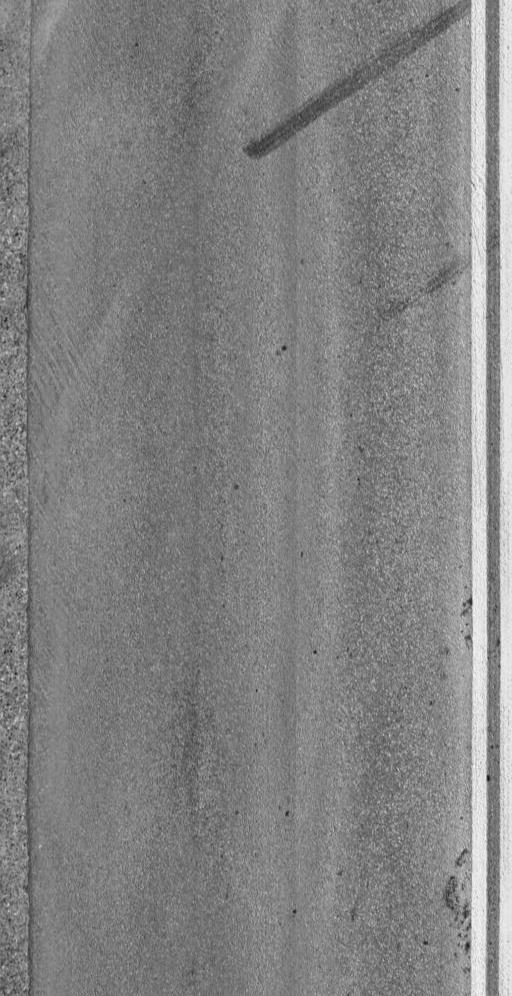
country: US
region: Vermont
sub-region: Rutland County
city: Rutland
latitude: 43.5771
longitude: -72.9516
